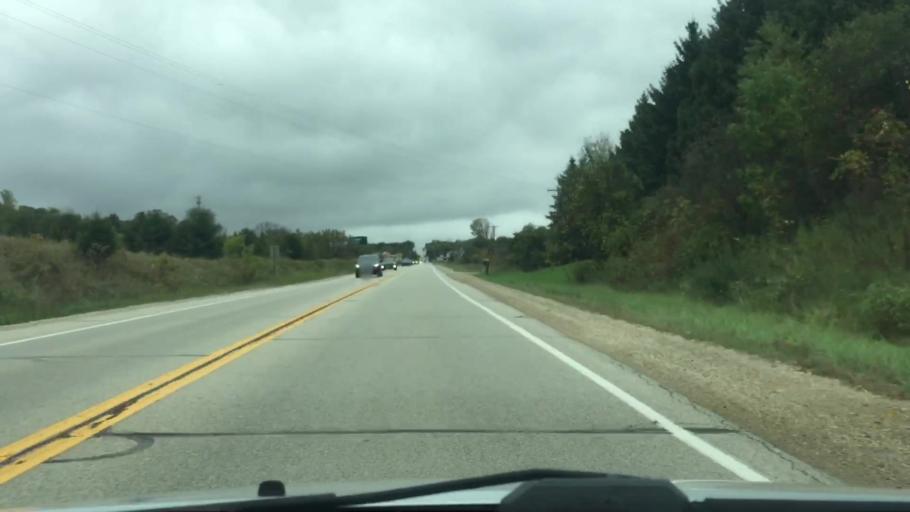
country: US
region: Wisconsin
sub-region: Walworth County
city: Elkhorn
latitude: 42.7310
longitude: -88.5429
